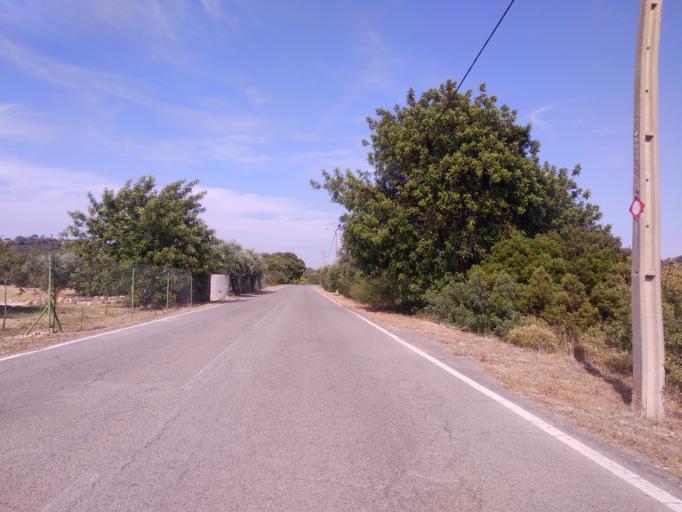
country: PT
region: Faro
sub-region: Sao Bras de Alportel
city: Sao Bras de Alportel
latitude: 37.1644
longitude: -7.9212
